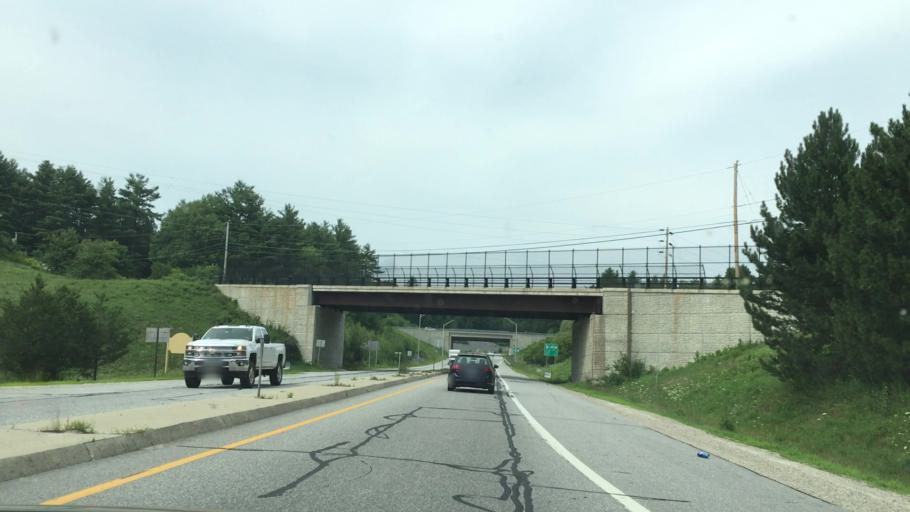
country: US
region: New Hampshire
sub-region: Hillsborough County
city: Hillsborough
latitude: 43.1132
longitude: -71.9187
